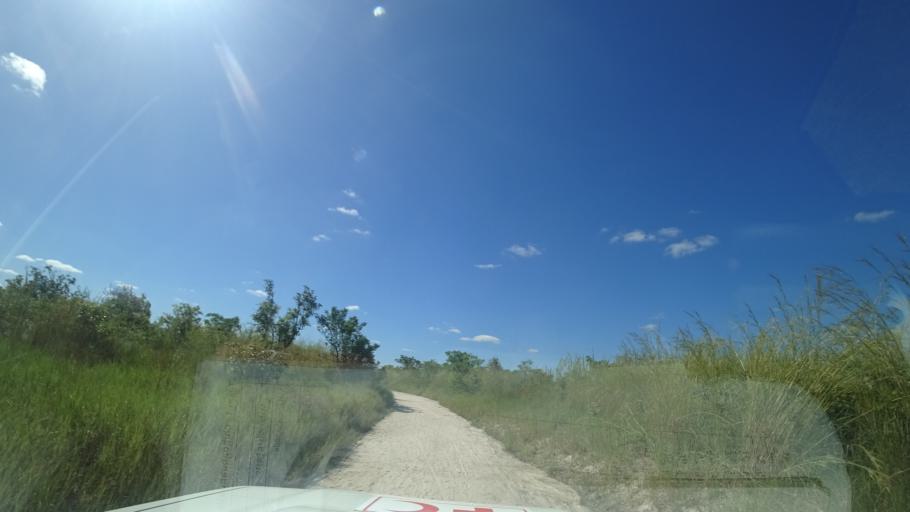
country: MZ
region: Sofala
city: Dondo
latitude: -19.4805
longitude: 34.6260
